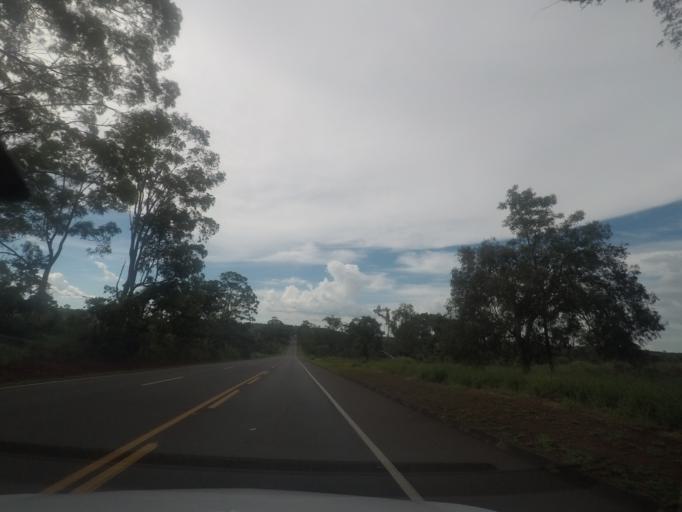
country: BR
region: Minas Gerais
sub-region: Prata
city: Prata
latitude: -19.2777
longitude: -48.9163
